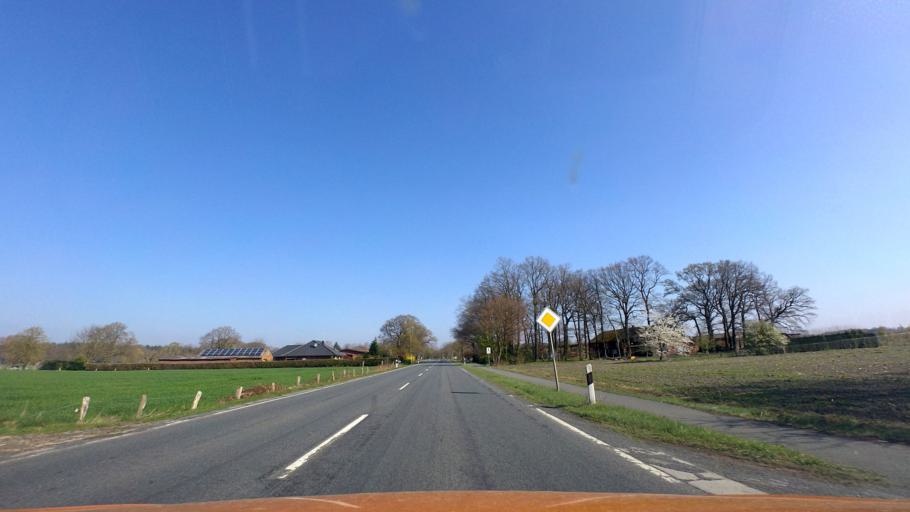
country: DE
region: Lower Saxony
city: Wardenburg
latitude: 53.0198
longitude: 8.1999
